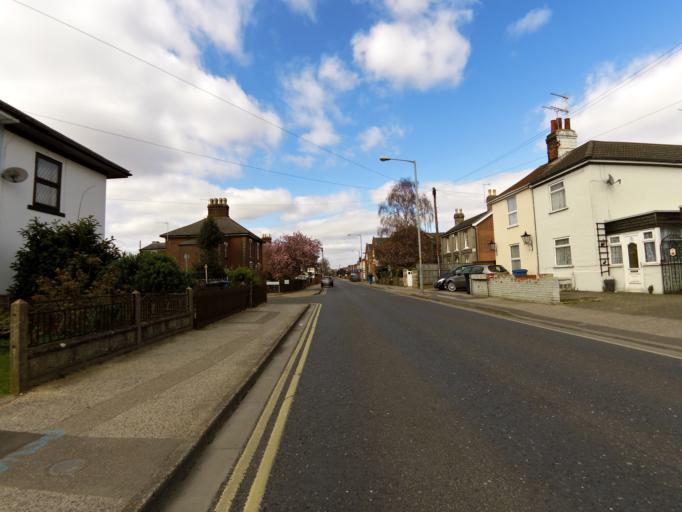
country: GB
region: England
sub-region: Suffolk
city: Ipswich
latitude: 52.0581
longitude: 1.1824
